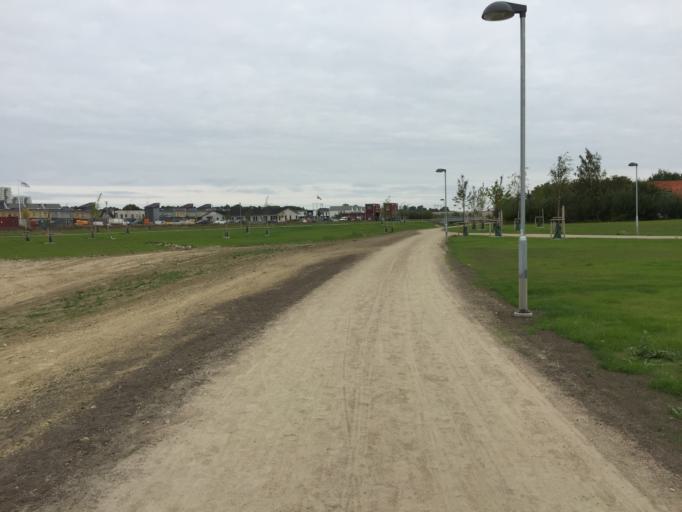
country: SE
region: Skane
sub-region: Lunds Kommun
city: Lund
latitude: 55.6887
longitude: 13.2299
